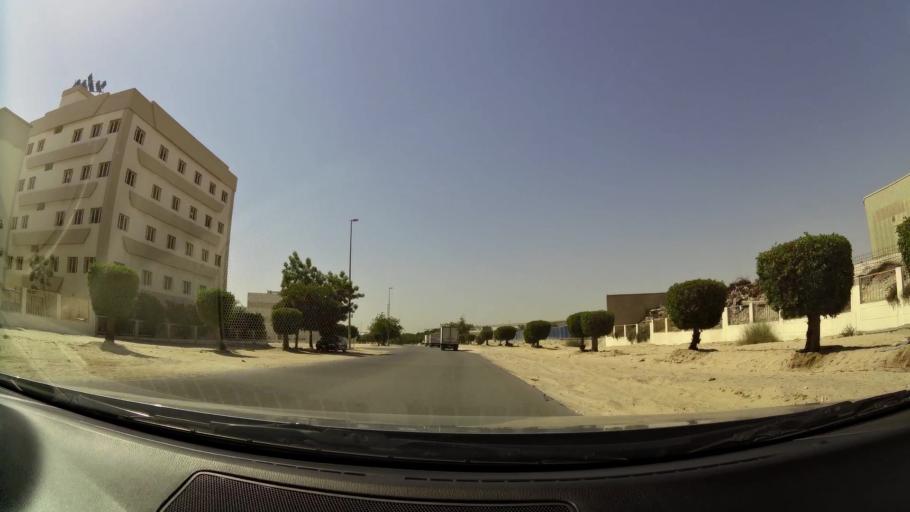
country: AE
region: Dubai
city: Dubai
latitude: 24.9734
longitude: 55.1722
